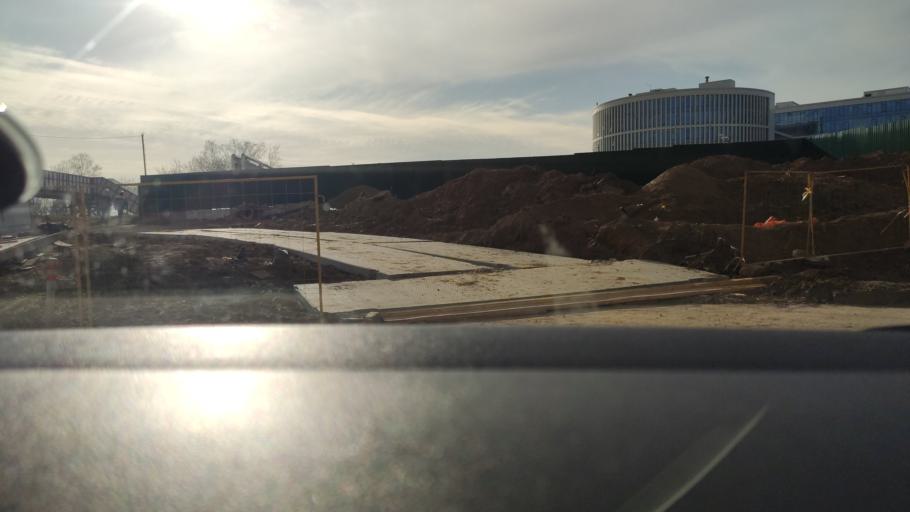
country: RU
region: Moskovskaya
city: Kommunarka
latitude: 55.5725
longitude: 37.4685
